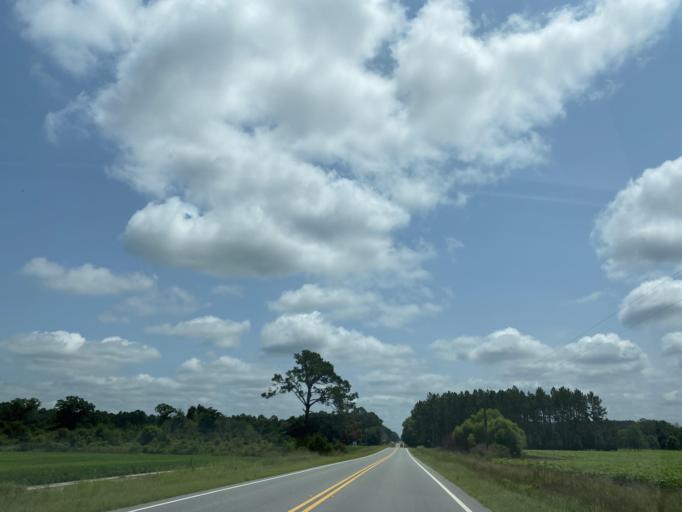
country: US
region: Georgia
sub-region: Jeff Davis County
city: Hazlehurst
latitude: 31.7175
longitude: -82.5234
